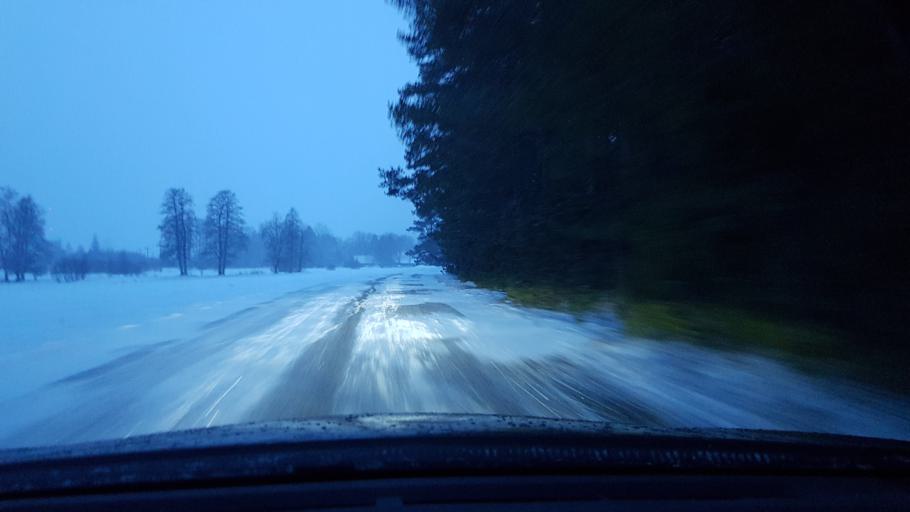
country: EE
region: Harju
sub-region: Kuusalu vald
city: Kuusalu
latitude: 59.4450
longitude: 25.5505
